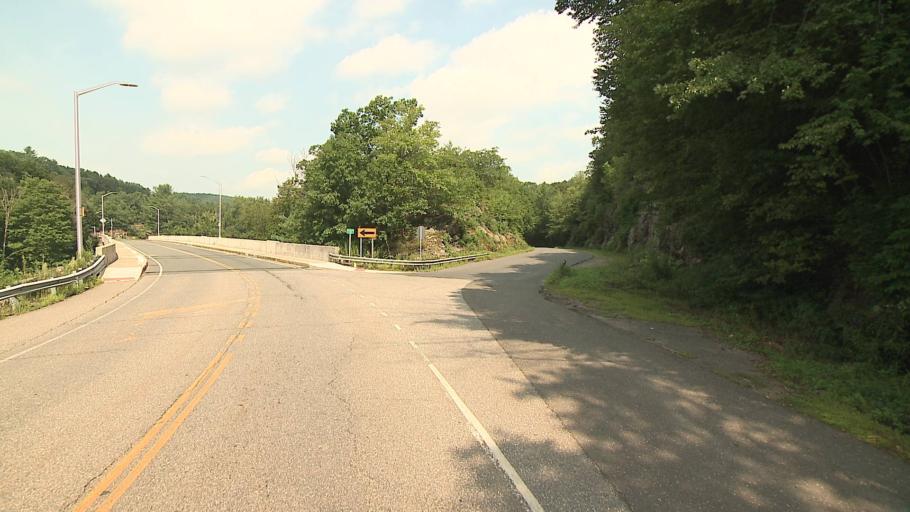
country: US
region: Connecticut
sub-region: Litchfield County
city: Thomaston
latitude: 41.6523
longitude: -73.0762
